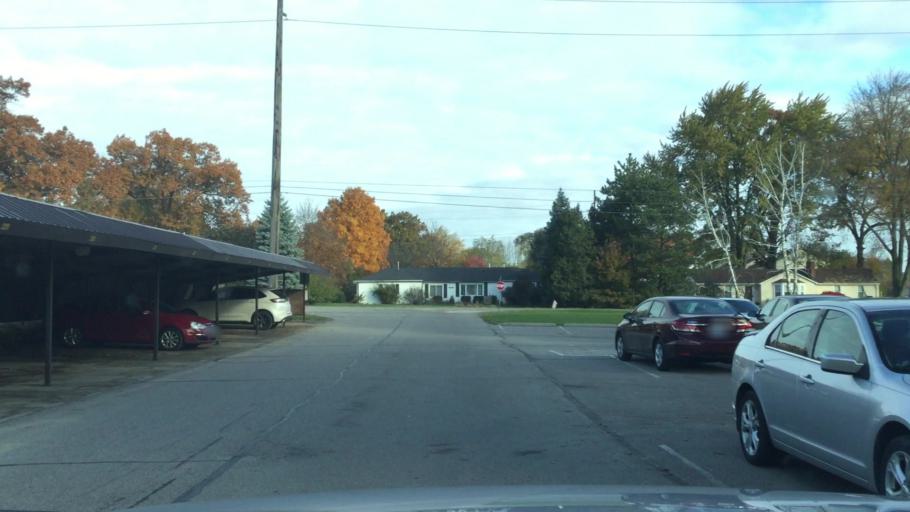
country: US
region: Michigan
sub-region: Wayne County
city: Westland
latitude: 42.3522
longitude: -83.4177
